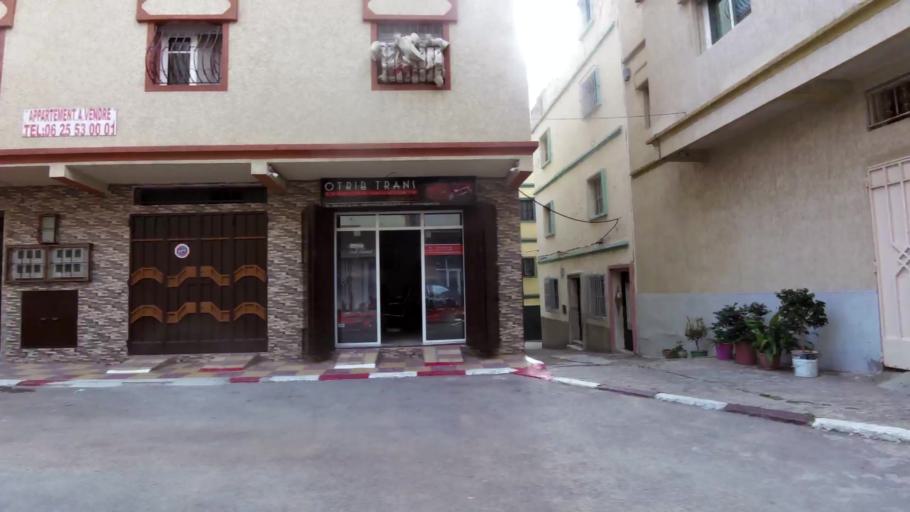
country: MA
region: Tanger-Tetouan
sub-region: Tanger-Assilah
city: Tangier
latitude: 35.7633
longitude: -5.8022
